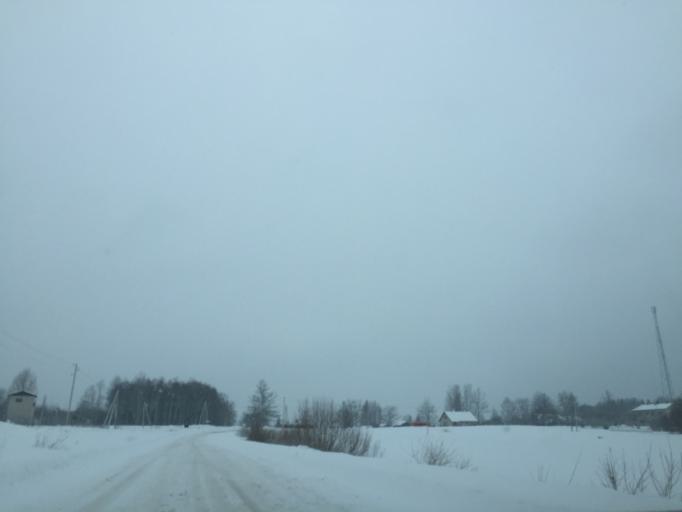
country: LV
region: Amatas Novads
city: Drabesi
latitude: 57.1669
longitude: 25.3281
